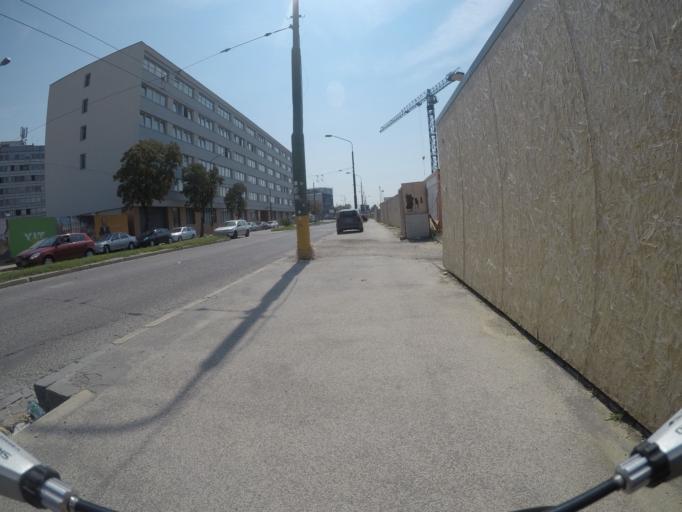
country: SK
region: Bratislavsky
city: Bratislava
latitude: 48.1470
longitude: 17.1310
